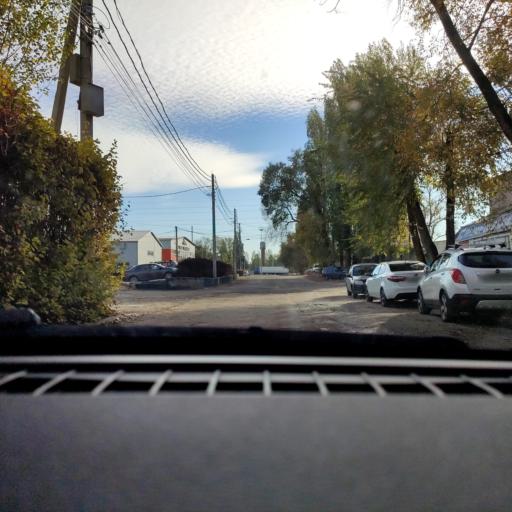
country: RU
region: Voronezj
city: Maslovka
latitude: 51.6469
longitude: 39.2947
